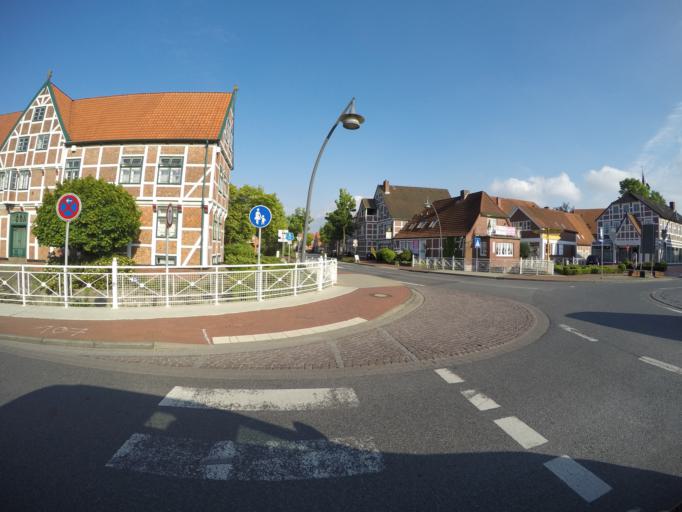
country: DE
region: Lower Saxony
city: Nottensdorf
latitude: 53.4849
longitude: 9.6433
